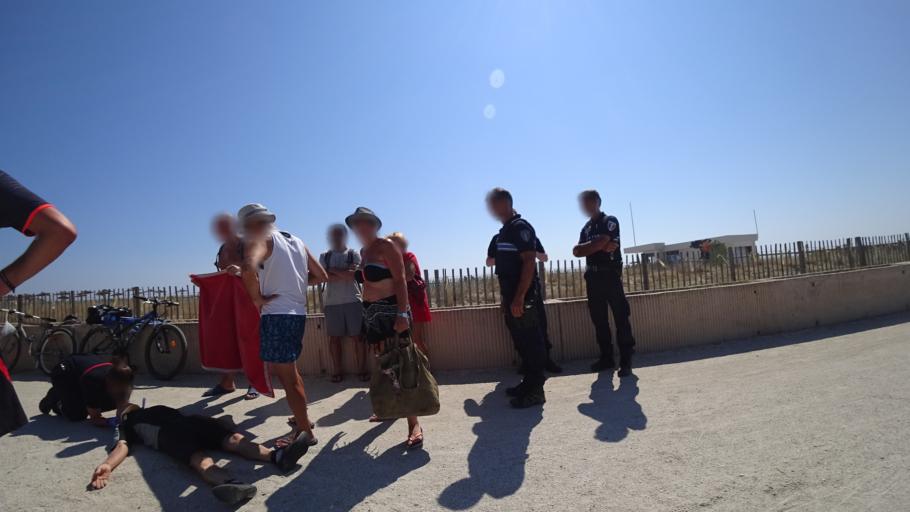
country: FR
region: Languedoc-Roussillon
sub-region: Departement des Pyrenees-Orientales
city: Le Barcares
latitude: 42.7825
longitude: 3.0380
